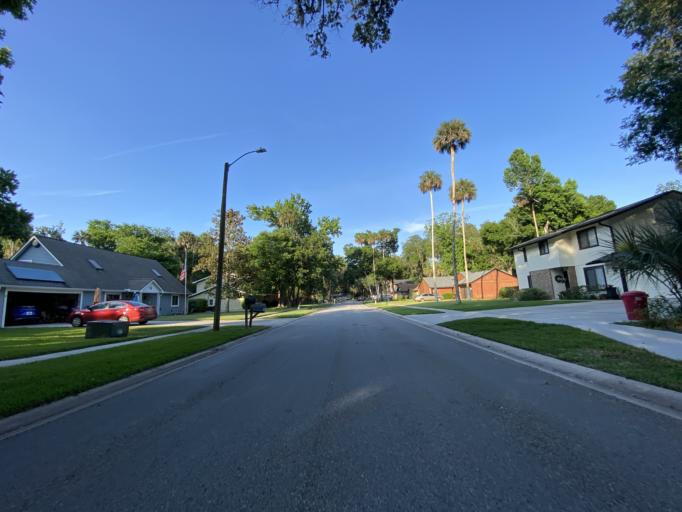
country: US
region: Florida
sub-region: Volusia County
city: Port Orange
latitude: 29.1437
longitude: -81.0106
